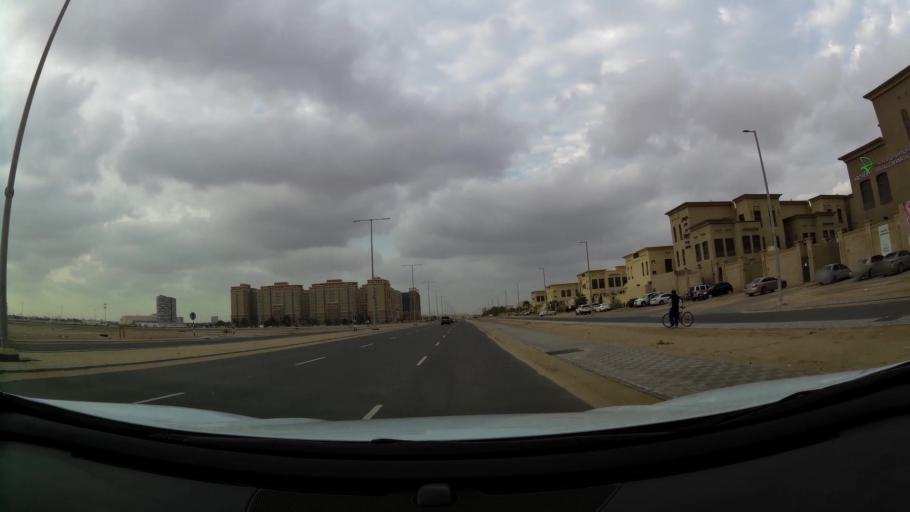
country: AE
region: Abu Dhabi
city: Abu Dhabi
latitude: 24.3661
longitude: 54.5399
